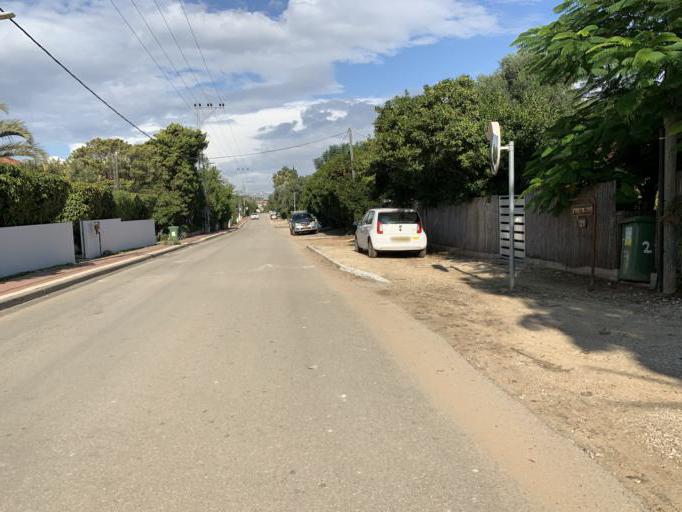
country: IL
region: Central District
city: Ra'anana
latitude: 32.1686
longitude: 34.8753
